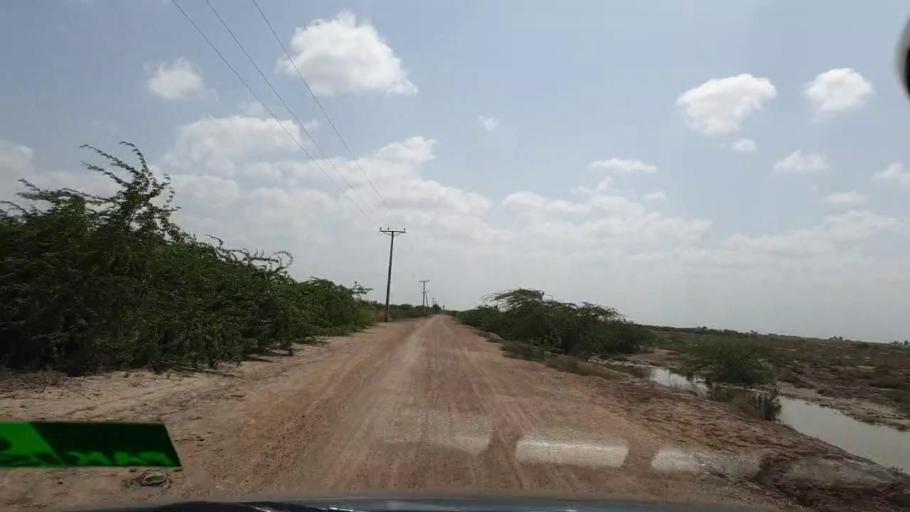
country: PK
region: Sindh
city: Kadhan
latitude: 24.6021
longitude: 69.1852
